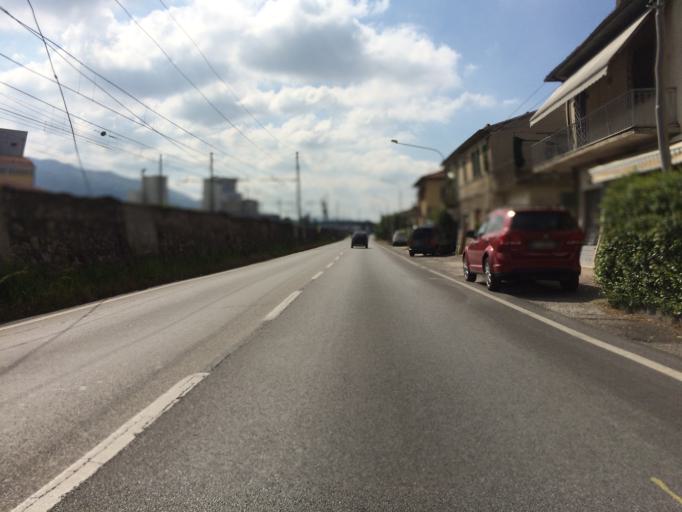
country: IT
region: Tuscany
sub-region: Provincia di Lucca
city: Strettoia
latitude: 43.9821
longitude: 10.1933
